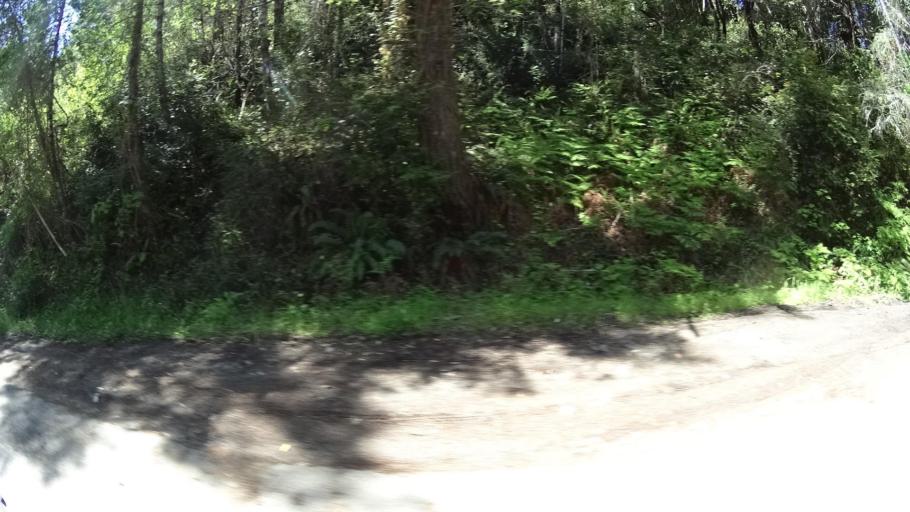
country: US
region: California
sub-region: Humboldt County
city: Rio Dell
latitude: 40.2301
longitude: -124.1511
